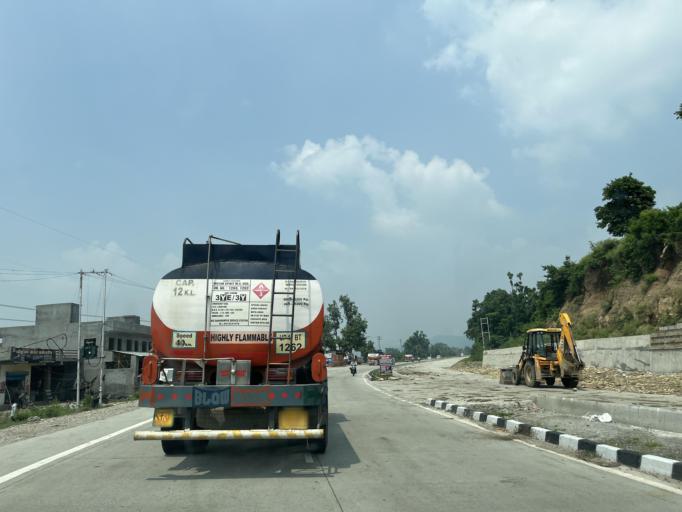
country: IN
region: Uttarakhand
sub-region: Haridwar
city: Haridwar
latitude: 29.8484
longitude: 78.1853
